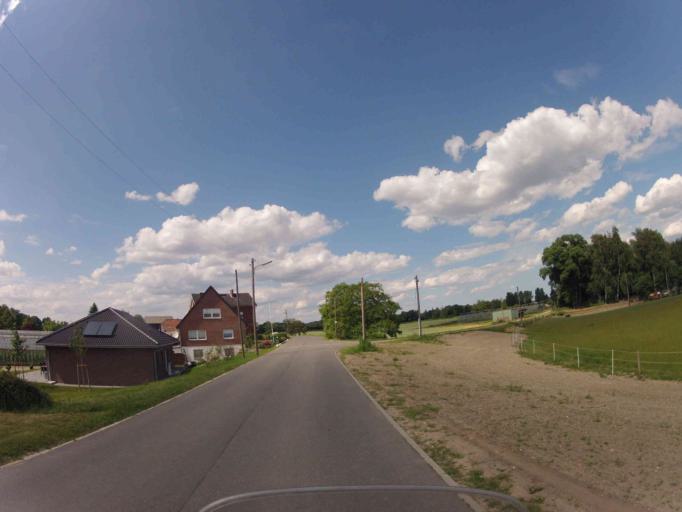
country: DE
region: Lower Saxony
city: Stelle
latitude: 53.4659
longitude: 10.1126
